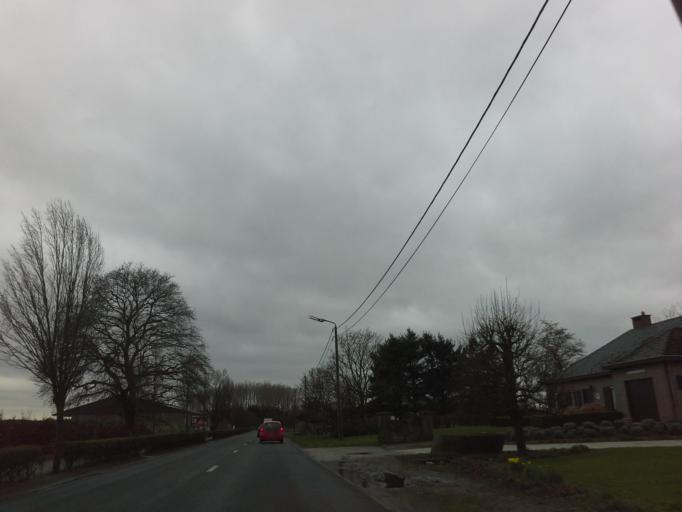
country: BE
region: Flanders
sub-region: Provincie Antwerpen
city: Hulshout
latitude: 51.1150
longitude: 4.8123
